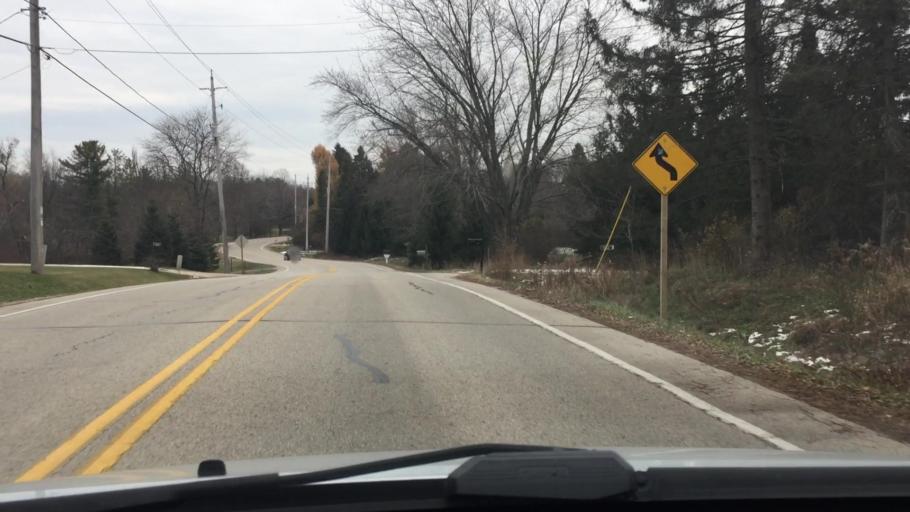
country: US
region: Wisconsin
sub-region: Ozaukee County
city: Grafton
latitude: 43.3002
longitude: -87.9608
